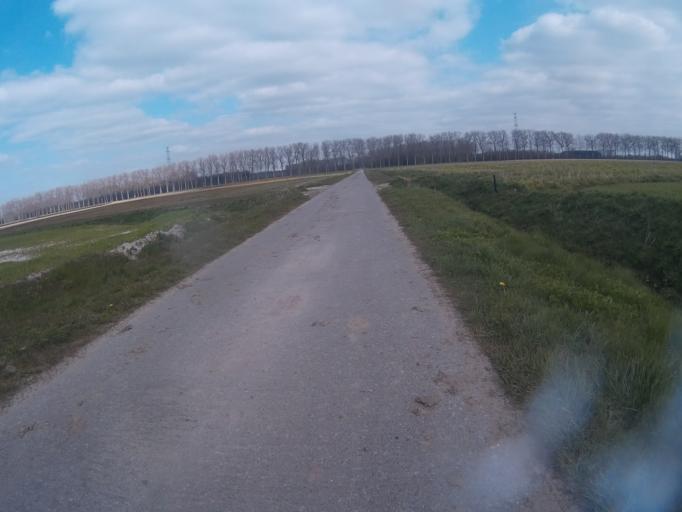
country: BE
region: Flanders
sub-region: Provincie Oost-Vlaanderen
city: Zomergem
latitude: 51.1502
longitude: 3.5467
